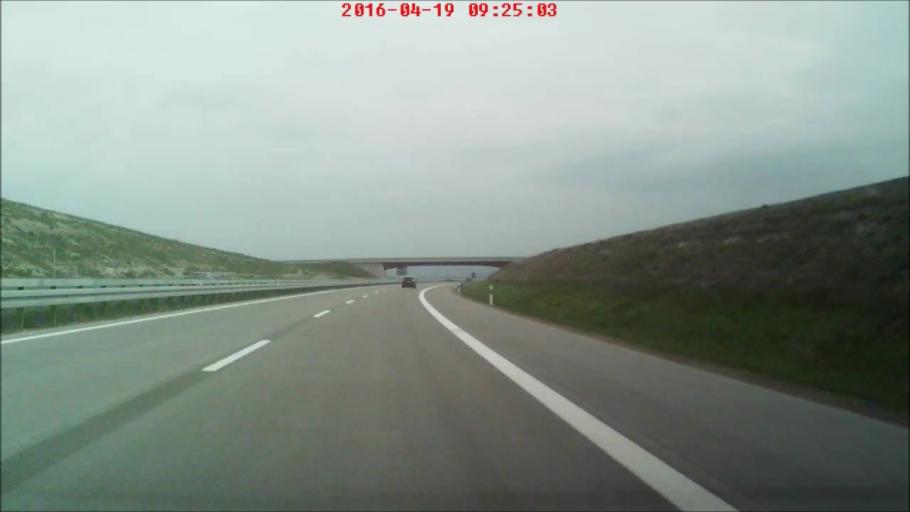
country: DE
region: Thuringia
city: Griefstedt
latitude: 51.1882
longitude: 11.1606
